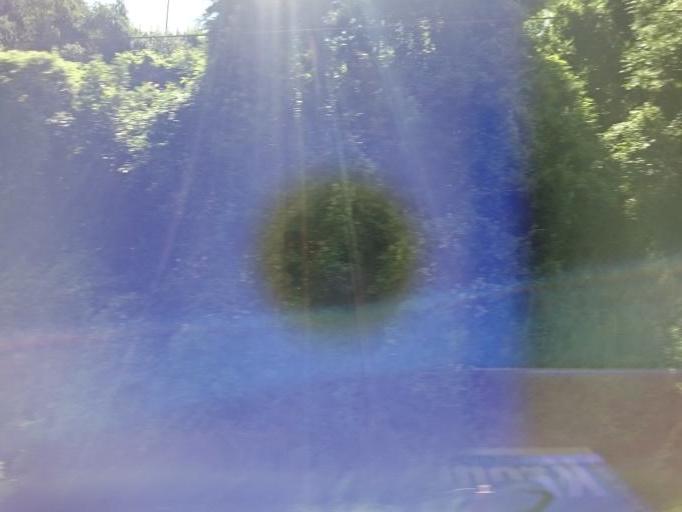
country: IT
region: Trentino-Alto Adige
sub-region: Bolzano
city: Velturno
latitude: 46.6502
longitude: 11.5879
